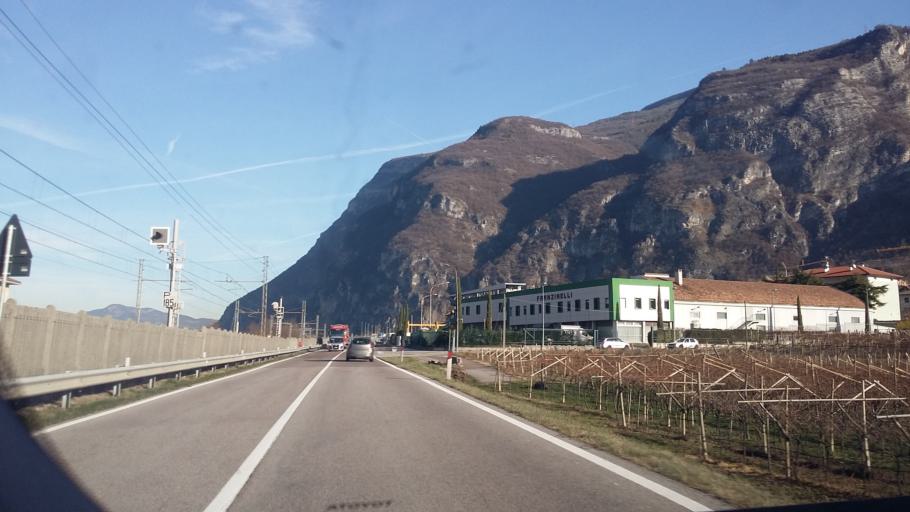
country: IT
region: Trentino-Alto Adige
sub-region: Provincia di Trento
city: Besenello
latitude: 45.9445
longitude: 11.1026
